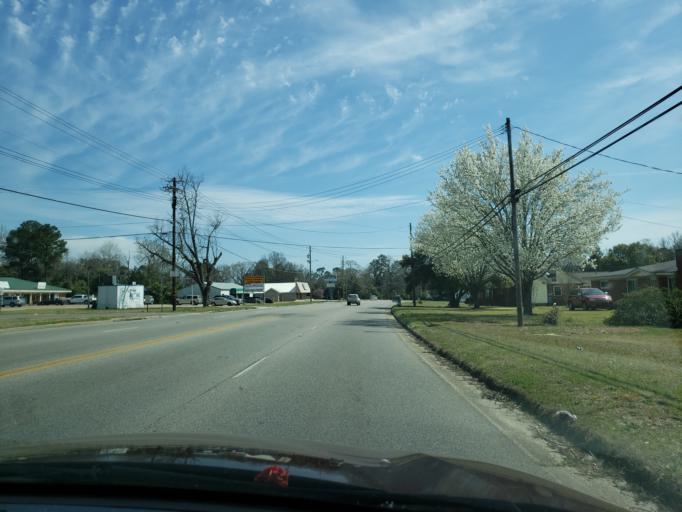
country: US
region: Alabama
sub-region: Elmore County
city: Tallassee
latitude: 32.5488
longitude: -85.9140
